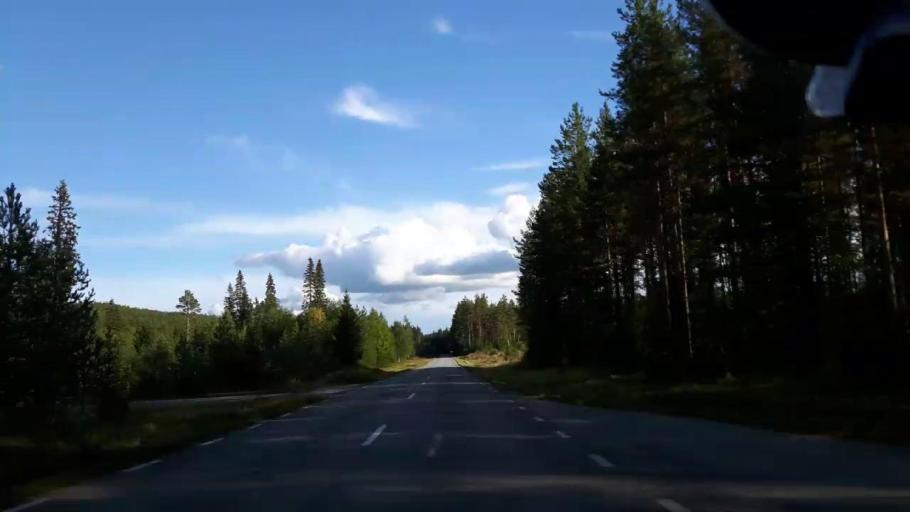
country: SE
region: Jaemtland
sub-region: Stroemsunds Kommun
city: Stroemsund
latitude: 63.4014
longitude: 15.5739
